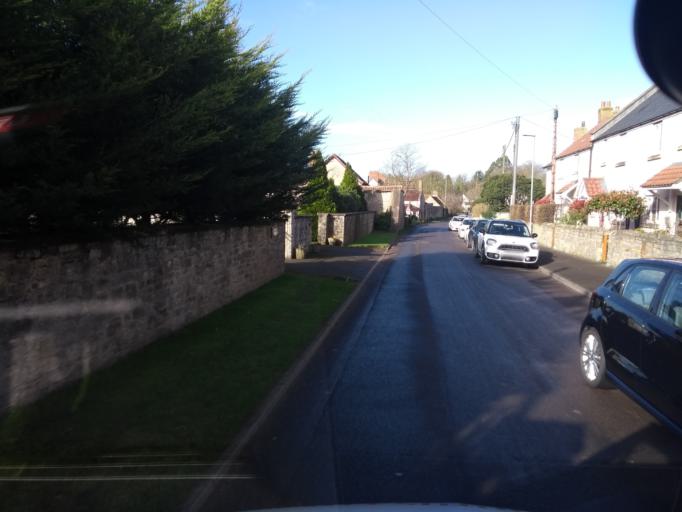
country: GB
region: England
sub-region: Somerset
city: Woolavington
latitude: 51.1572
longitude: -2.9178
